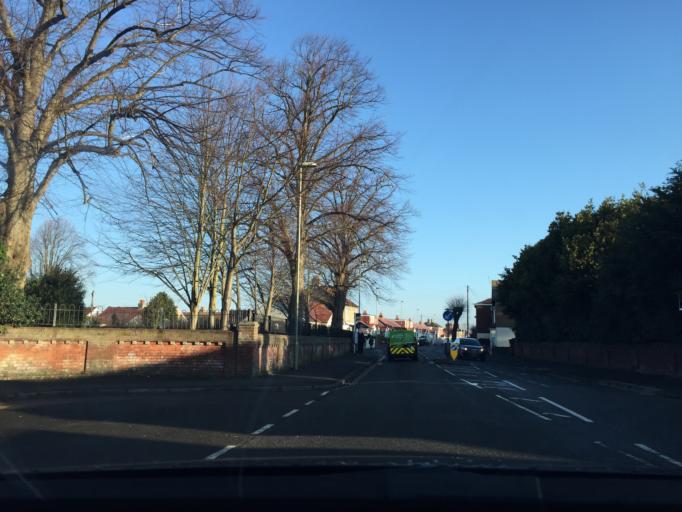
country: GB
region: England
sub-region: Hampshire
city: Gosport
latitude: 50.7980
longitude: -1.1488
